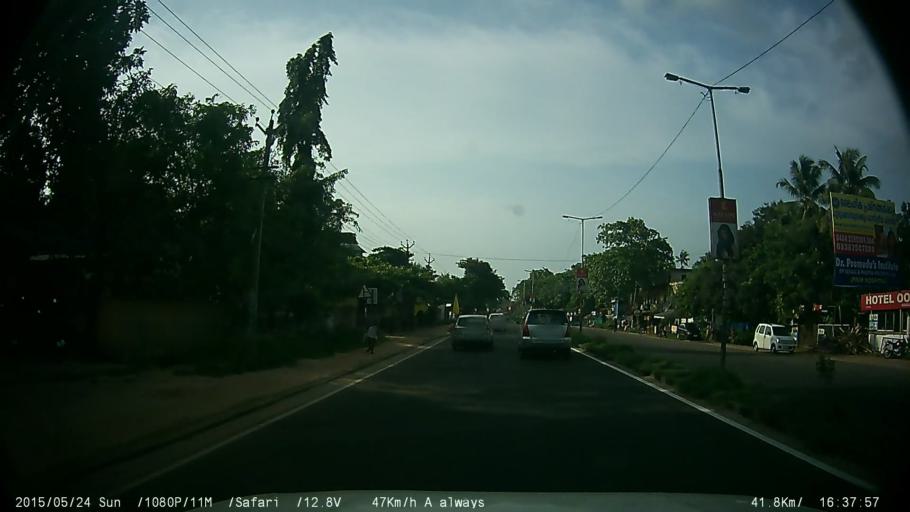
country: IN
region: Kerala
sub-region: Alappuzha
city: Shertallai
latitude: 9.6071
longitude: 76.3292
